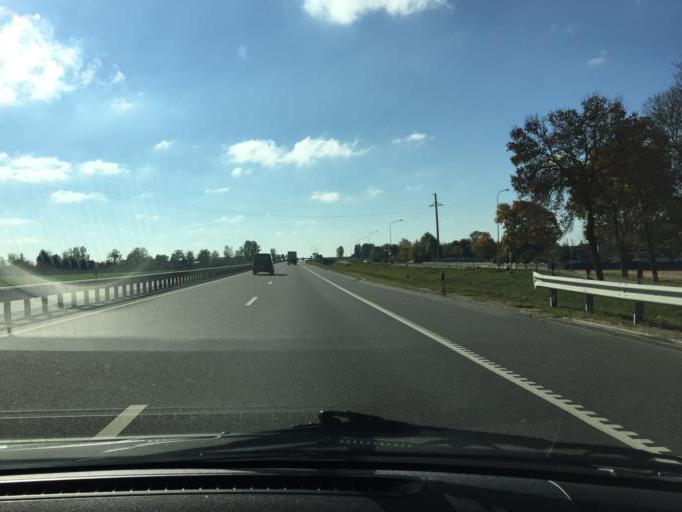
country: BY
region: Minsk
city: Slutsk
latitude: 53.0778
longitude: 27.5626
